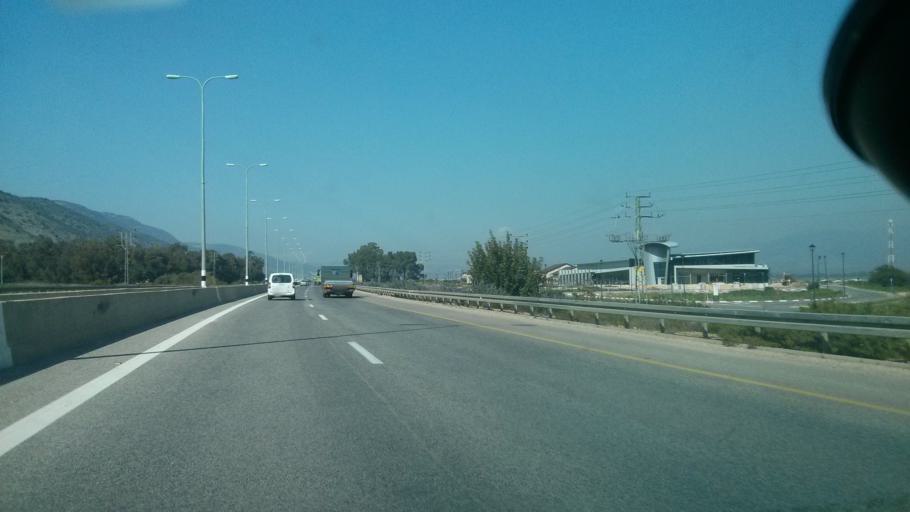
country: IL
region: Northern District
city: Qiryat Shemona
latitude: 33.1136
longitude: 35.5721
